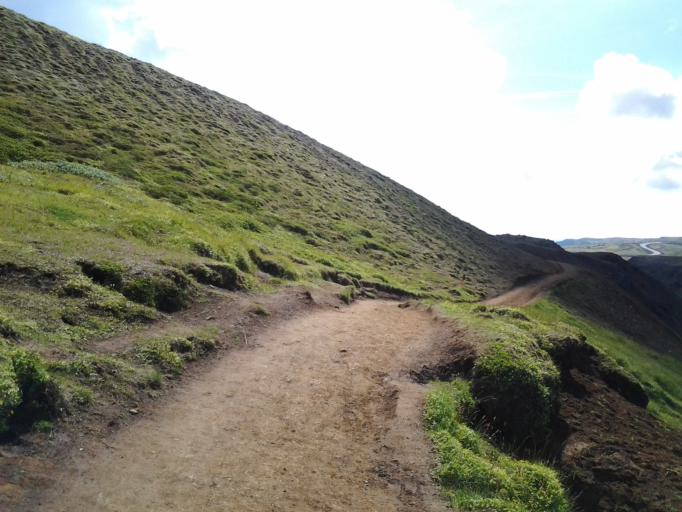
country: IS
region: South
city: Hveragerdi
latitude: 64.0356
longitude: -21.2187
